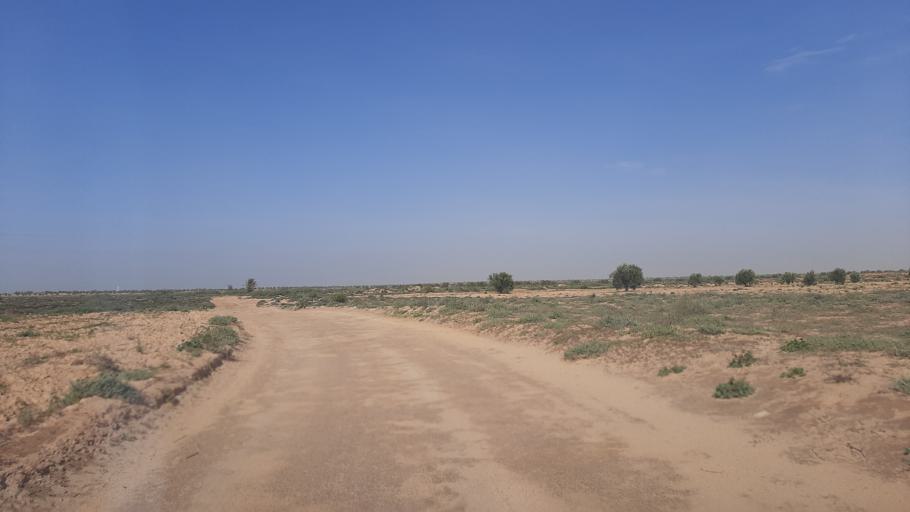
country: TN
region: Madanin
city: Zarzis
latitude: 33.4432
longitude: 10.8086
